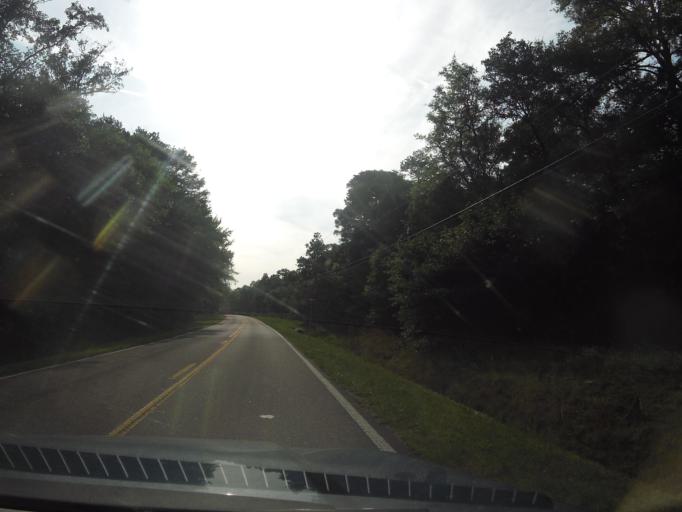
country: US
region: Florida
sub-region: Duval County
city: Atlantic Beach
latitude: 30.4621
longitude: -81.4872
